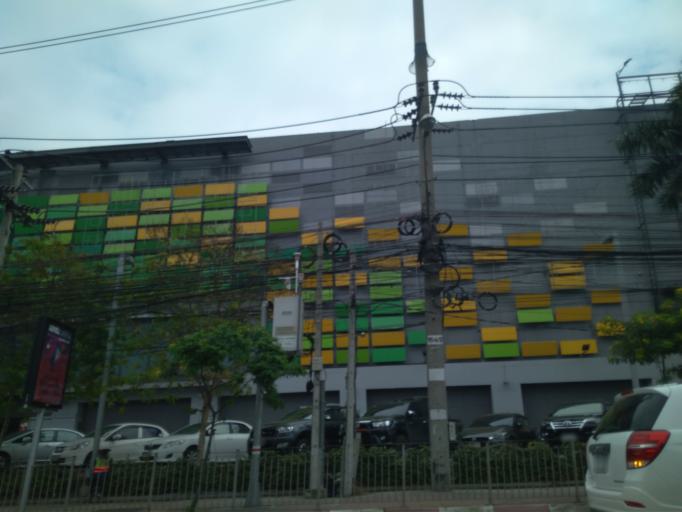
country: TH
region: Bangkok
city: Bang Na
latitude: 13.6961
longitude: 100.6475
